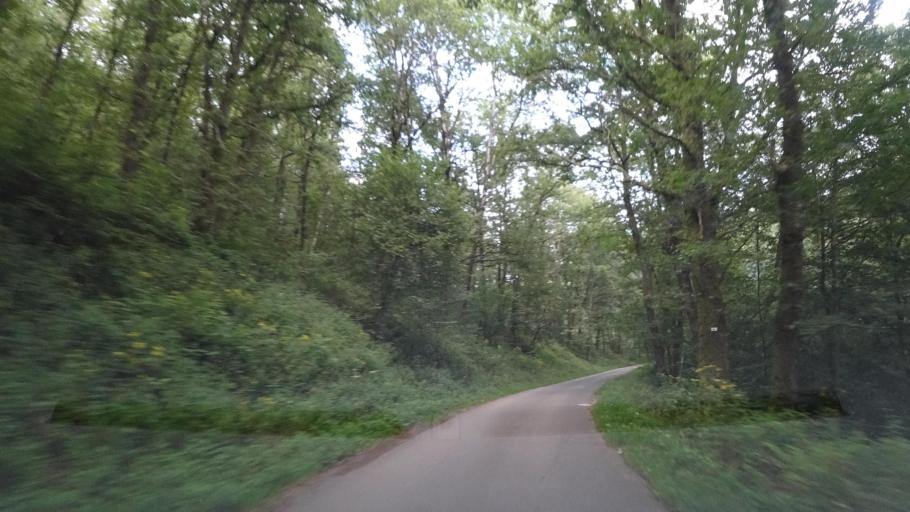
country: BE
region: Wallonia
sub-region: Province du Luxembourg
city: Herbeumont
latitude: 49.7765
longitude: 5.2559
